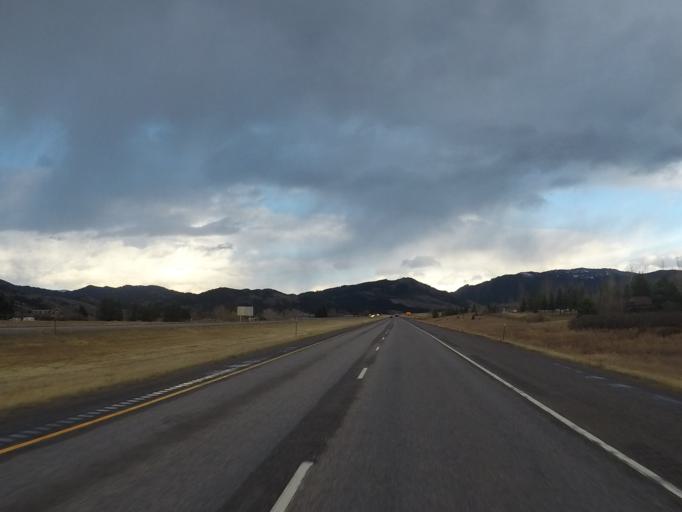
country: US
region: Montana
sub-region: Gallatin County
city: Bozeman
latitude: 45.6679
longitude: -110.9876
